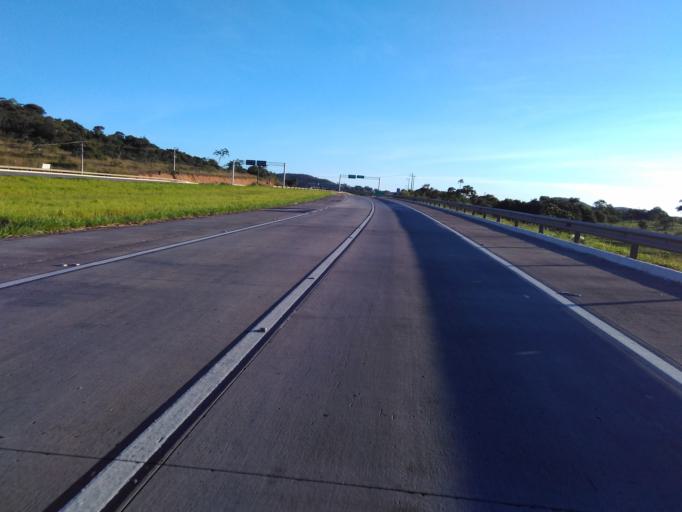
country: BR
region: Sergipe
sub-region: Nossa Senhora Do Socorro
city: Nossa Senhora do Socorro
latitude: -10.9186
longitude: -37.1689
